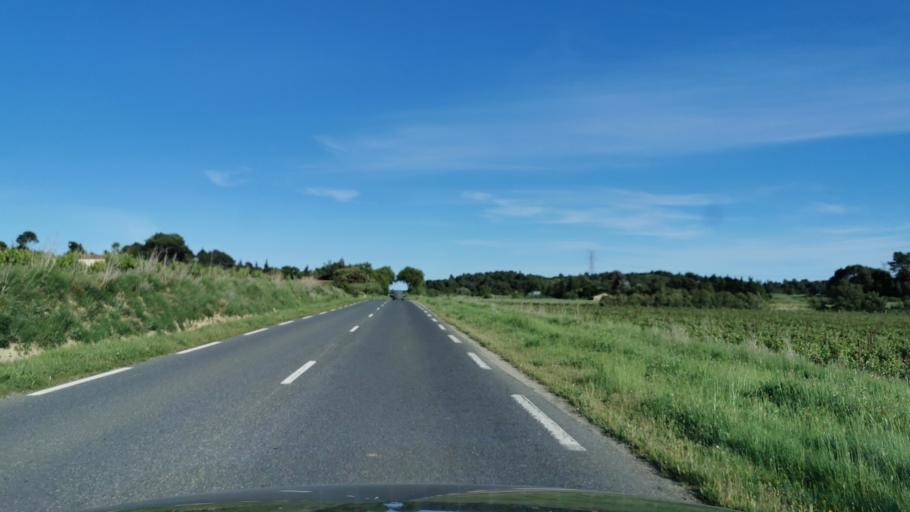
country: FR
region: Languedoc-Roussillon
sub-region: Departement de l'Aude
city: Moussan
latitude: 43.2086
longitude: 2.9505
